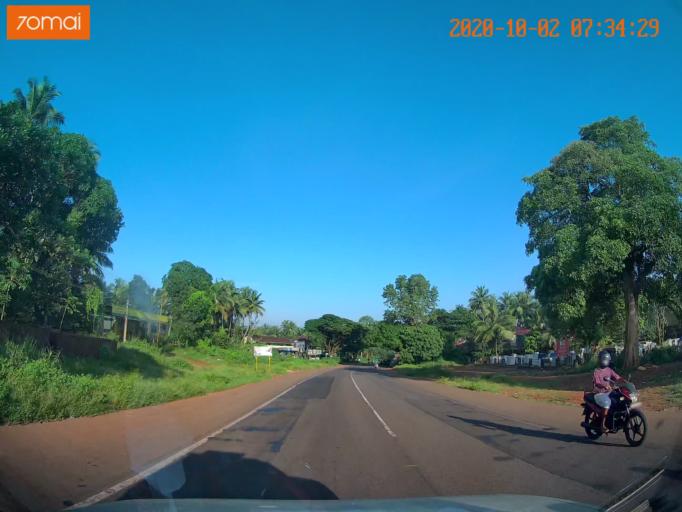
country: IN
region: Kerala
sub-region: Malappuram
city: Pariyapuram
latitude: 11.0634
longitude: 75.9293
